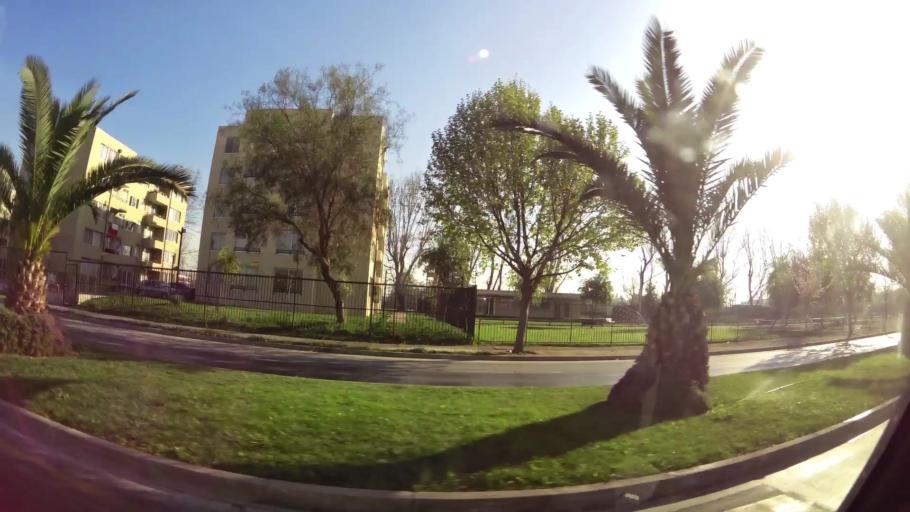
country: CL
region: Santiago Metropolitan
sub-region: Provincia de Santiago
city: Lo Prado
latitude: -33.4525
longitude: -70.7482
